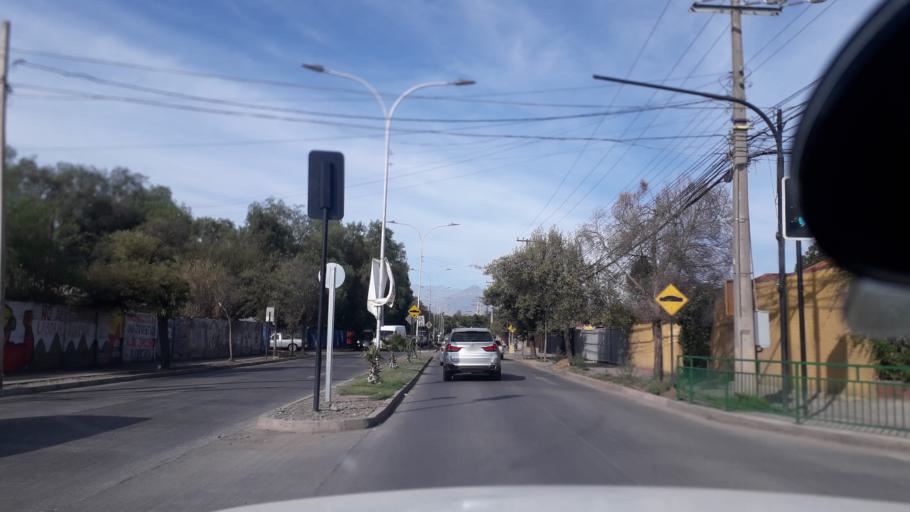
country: CL
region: Valparaiso
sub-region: Provincia de San Felipe
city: San Felipe
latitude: -32.7499
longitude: -70.7108
